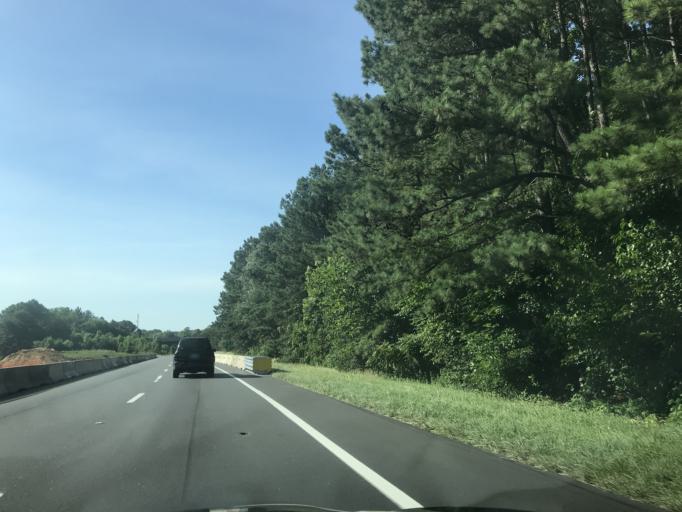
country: US
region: North Carolina
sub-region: Wake County
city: Garner
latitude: 35.7509
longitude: -78.5948
